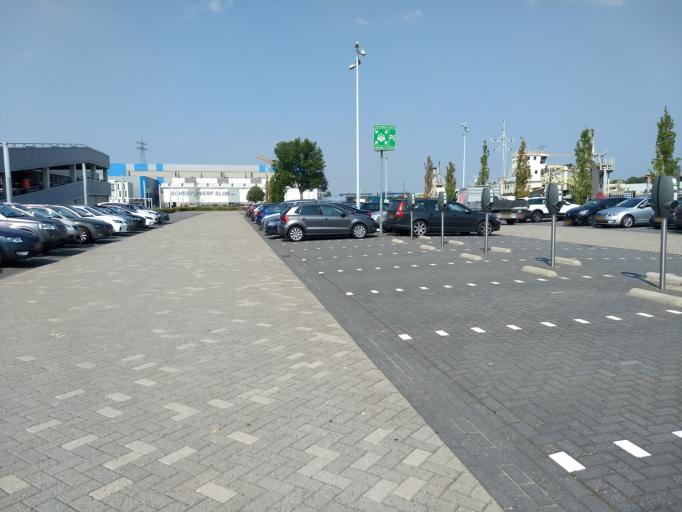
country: NL
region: South Holland
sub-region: Gemeente Papendrecht
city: Papendrecht
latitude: 51.8251
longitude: 4.7267
